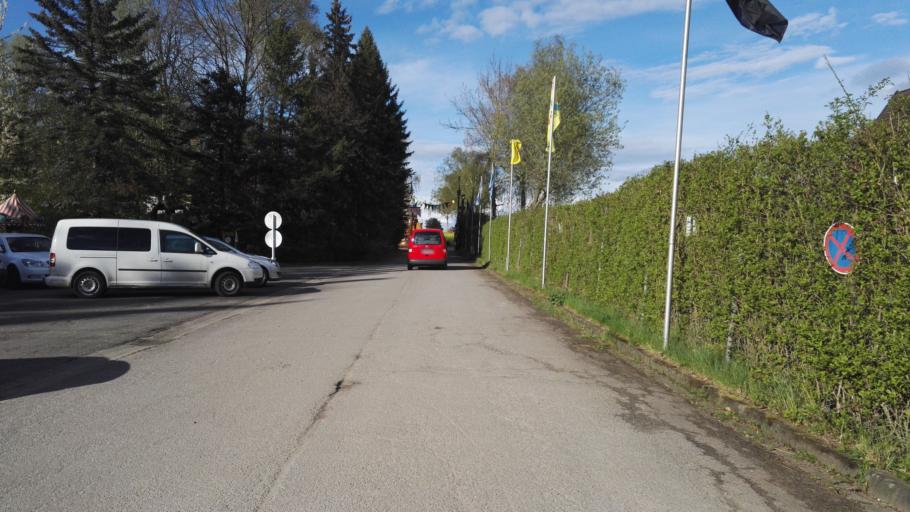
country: DE
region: Lower Saxony
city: Holle
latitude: 52.0723
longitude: 10.1392
